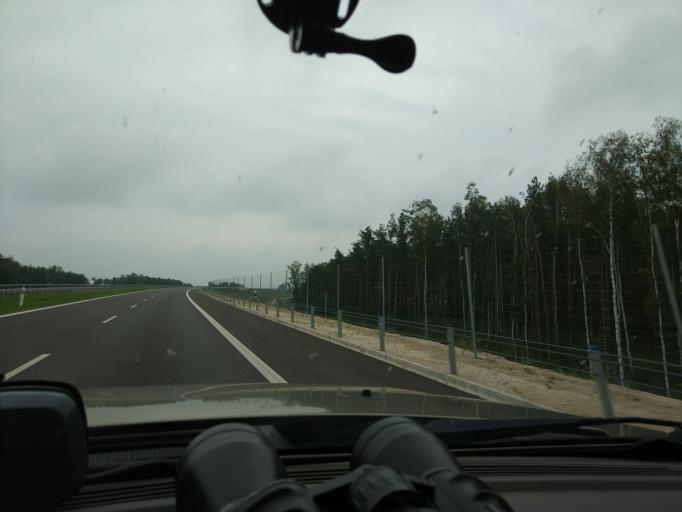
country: PL
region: Podlasie
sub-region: Powiat zambrowski
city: Szumowo
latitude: 52.9398
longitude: 22.1466
